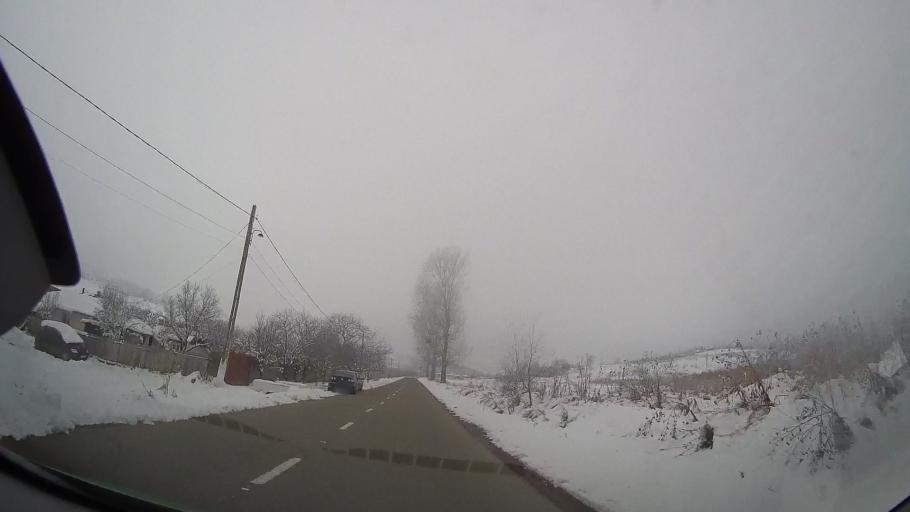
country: RO
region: Neamt
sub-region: Comuna Oniceni
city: Oniceni
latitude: 46.8005
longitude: 27.1212
